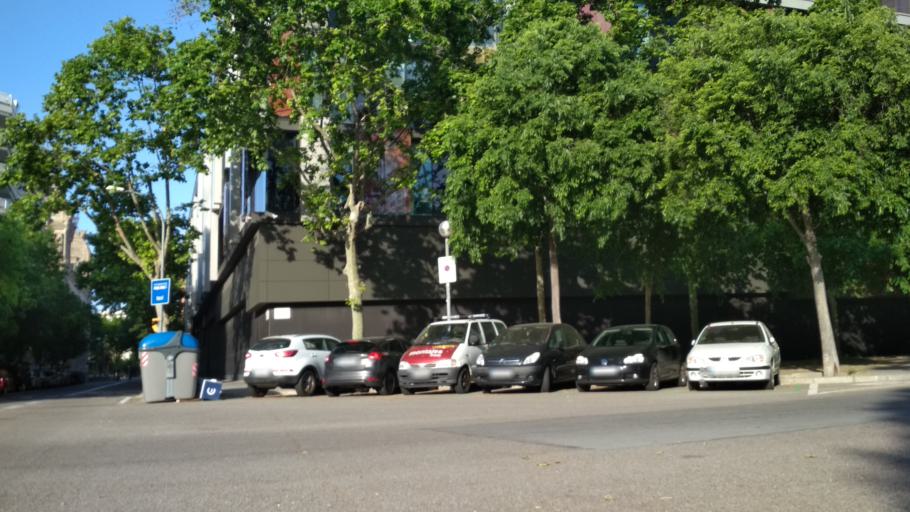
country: ES
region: Catalonia
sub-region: Provincia de Barcelona
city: Ciutat Vella
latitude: 41.3923
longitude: 2.1835
